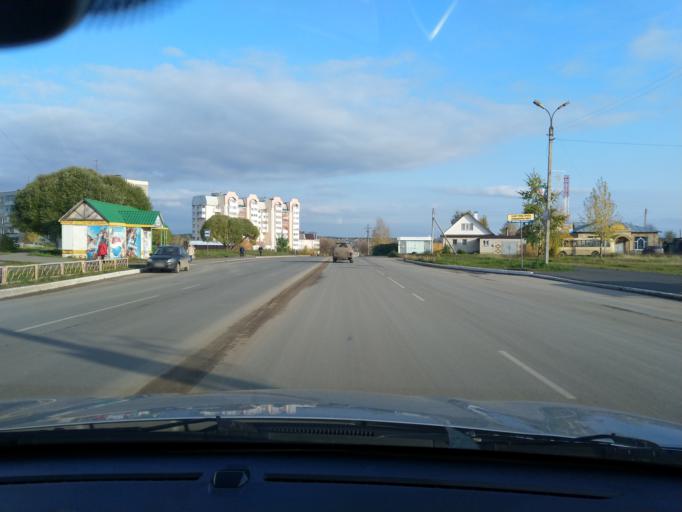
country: RU
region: Perm
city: Dobryanka
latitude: 58.4627
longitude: 56.4009
